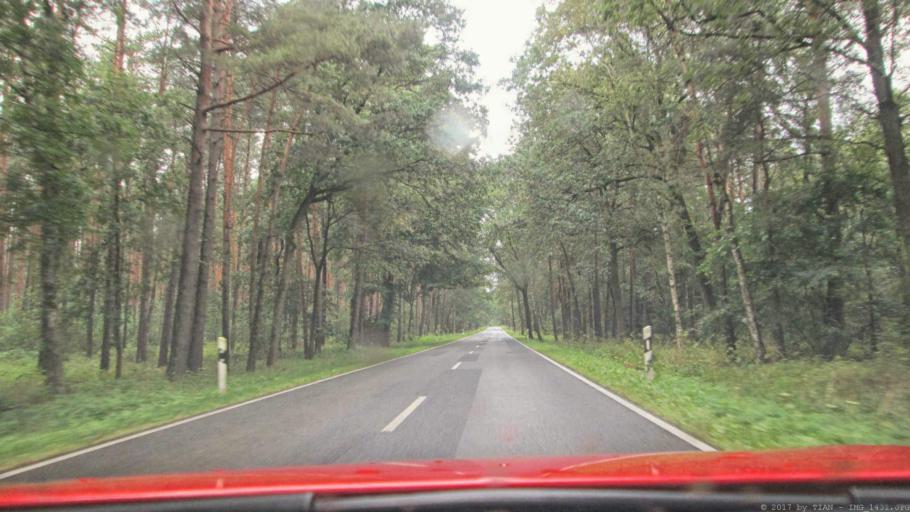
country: DE
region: Lower Saxony
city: Wittingen
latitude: 52.7778
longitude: 10.7143
